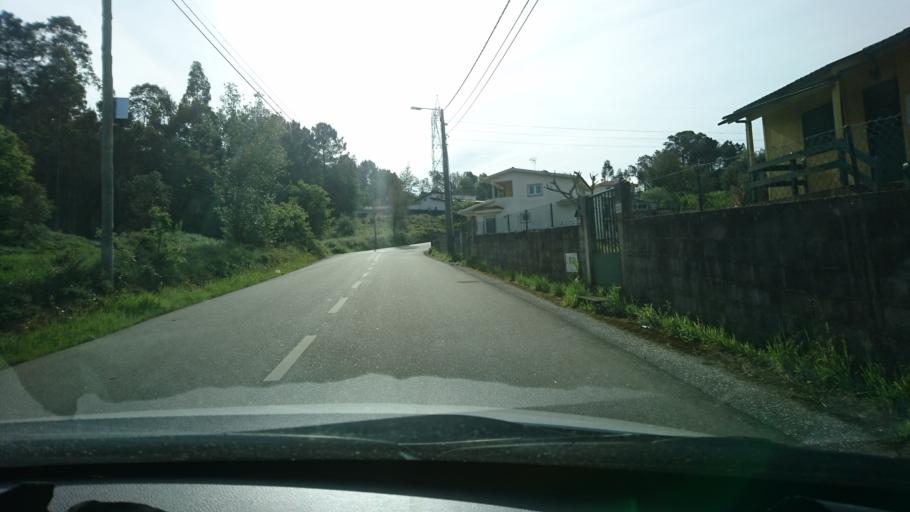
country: PT
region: Aveiro
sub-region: Oliveira de Azemeis
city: Sao Roque
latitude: 40.8789
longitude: -8.4798
